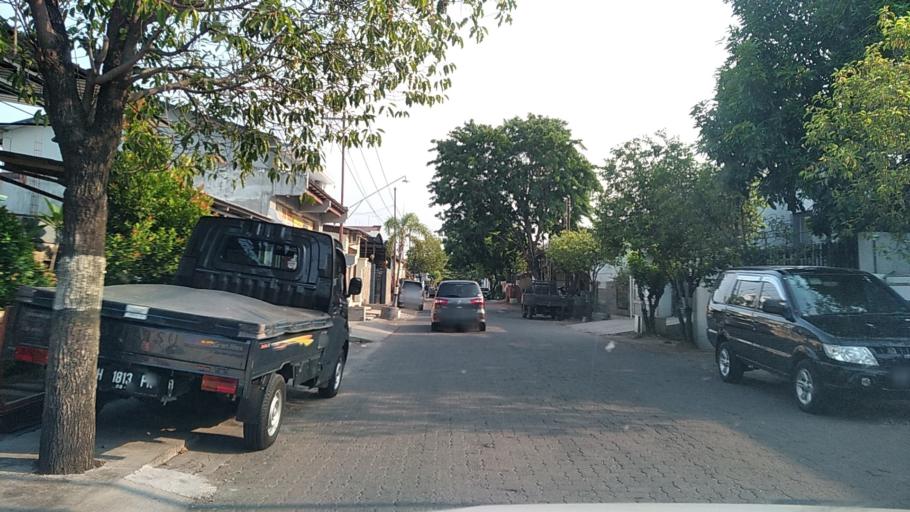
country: ID
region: Central Java
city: Semarang
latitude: -6.9623
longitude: 110.4052
